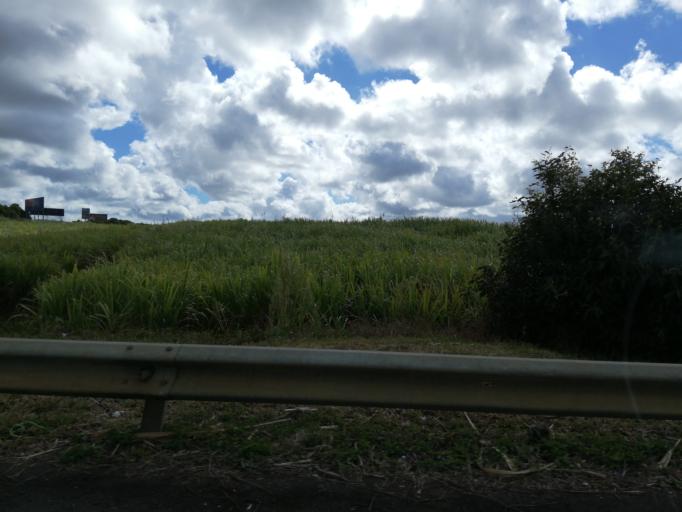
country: MU
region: Grand Port
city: Plaine Magnien
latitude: -20.4226
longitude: 57.6604
